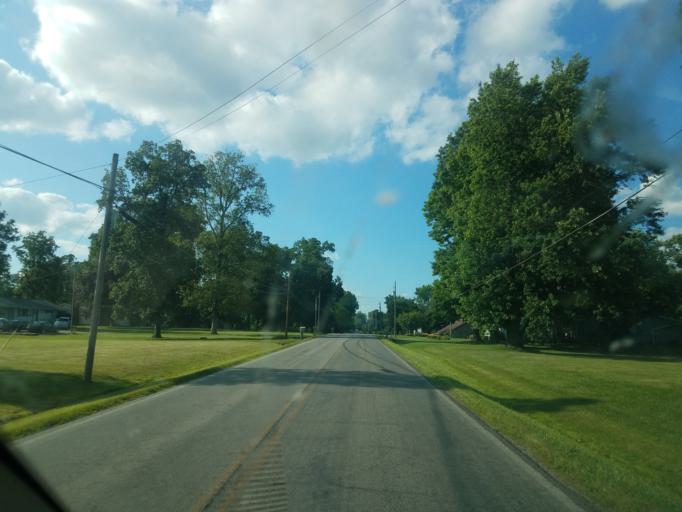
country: US
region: Ohio
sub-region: Wayne County
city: Apple Creek
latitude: 40.7570
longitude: -81.8959
